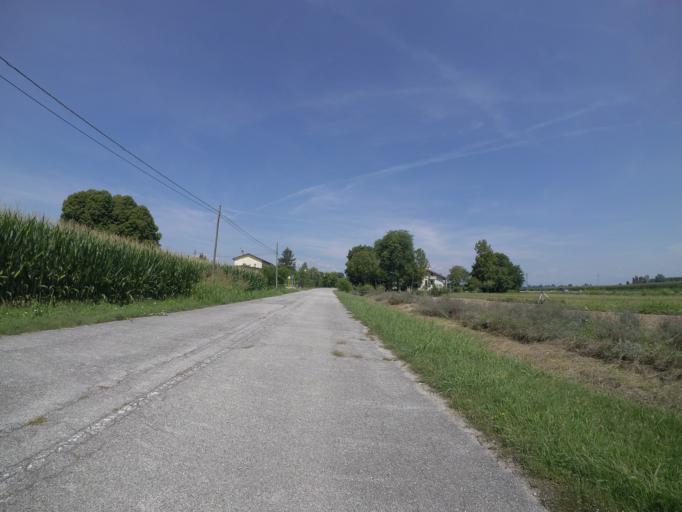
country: IT
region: Friuli Venezia Giulia
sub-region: Provincia di Udine
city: Varmo
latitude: 45.9170
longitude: 12.9948
